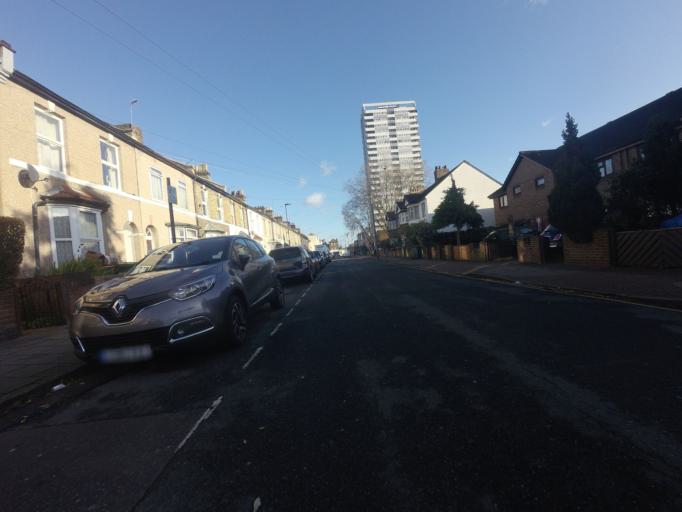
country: GB
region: England
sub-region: Greater London
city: Poplar
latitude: 51.5489
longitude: 0.0029
